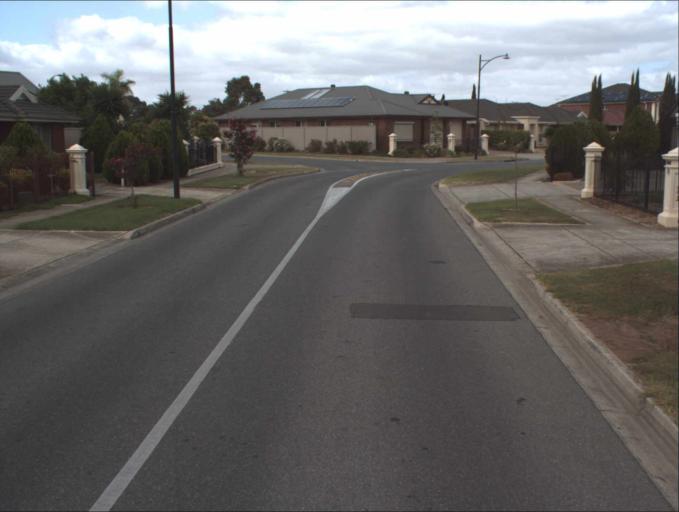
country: AU
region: South Australia
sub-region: Charles Sturt
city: Woodville
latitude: -34.8721
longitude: 138.5622
